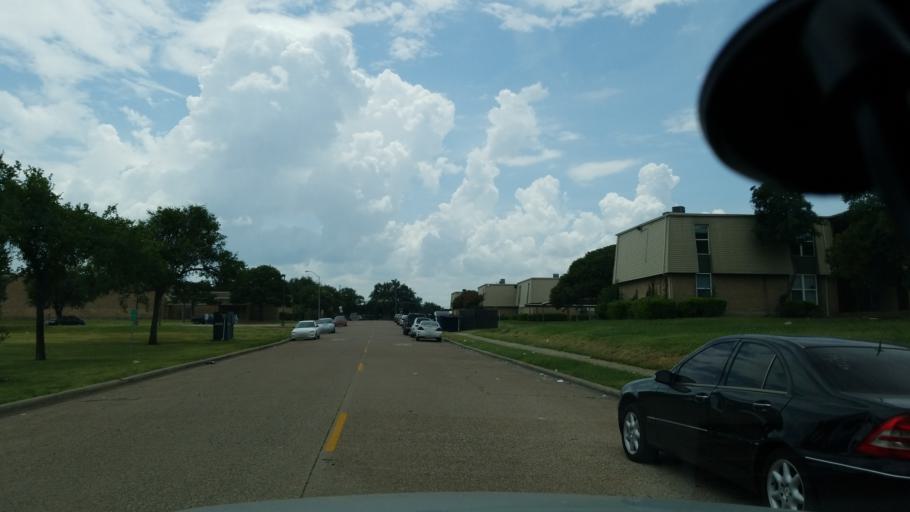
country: US
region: Texas
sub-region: Dallas County
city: Cockrell Hill
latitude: 32.6848
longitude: -96.8553
